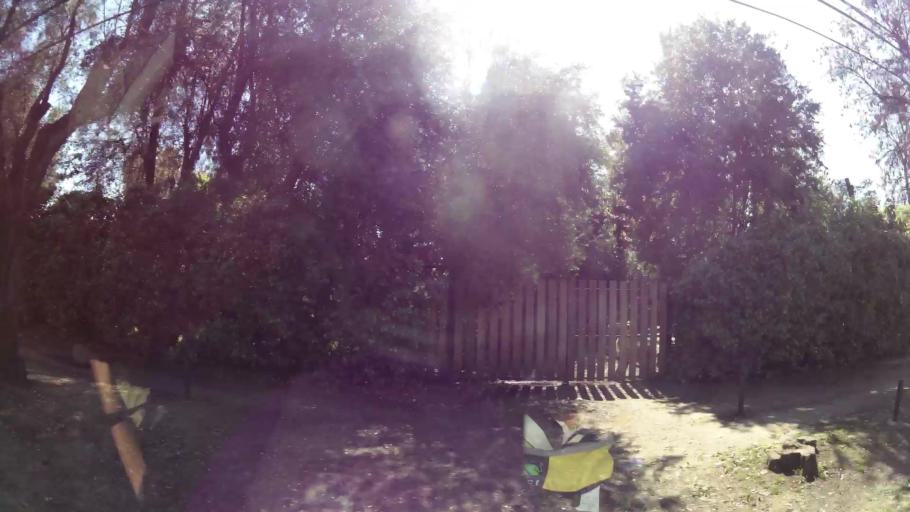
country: CL
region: Santiago Metropolitan
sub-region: Provincia de Santiago
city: Villa Presidente Frei, Nunoa, Santiago, Chile
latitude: -33.4424
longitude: -70.5256
